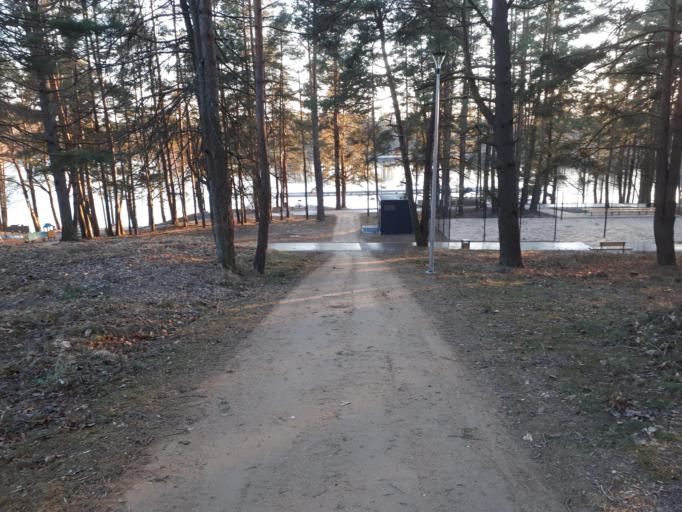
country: LT
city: Zarasai
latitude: 55.7278
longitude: 26.2514
